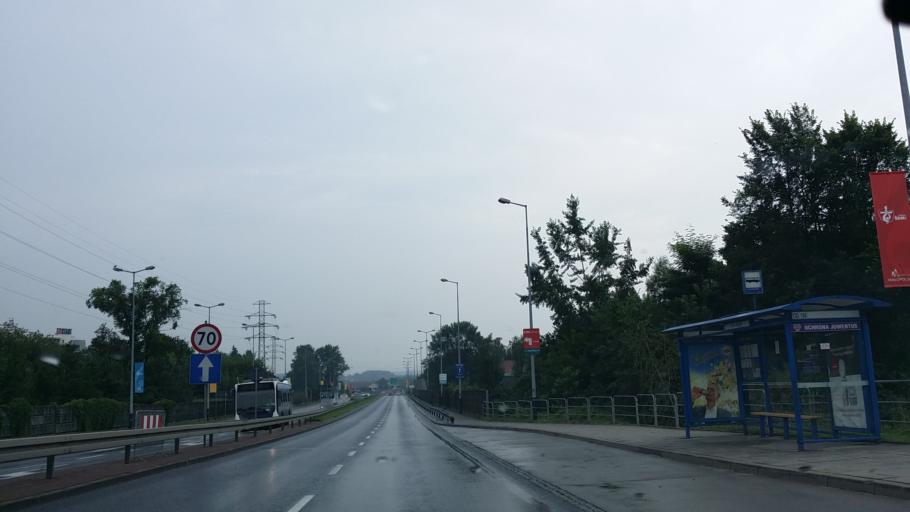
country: PL
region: Lesser Poland Voivodeship
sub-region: Krakow
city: Krakow
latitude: 50.0192
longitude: 19.9455
